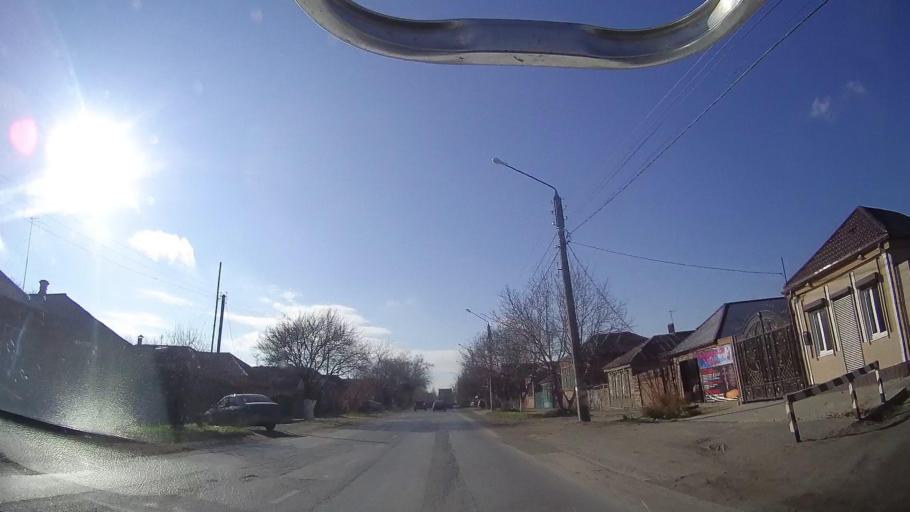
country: RU
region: Rostov
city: Bataysk
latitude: 47.1362
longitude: 39.7041
